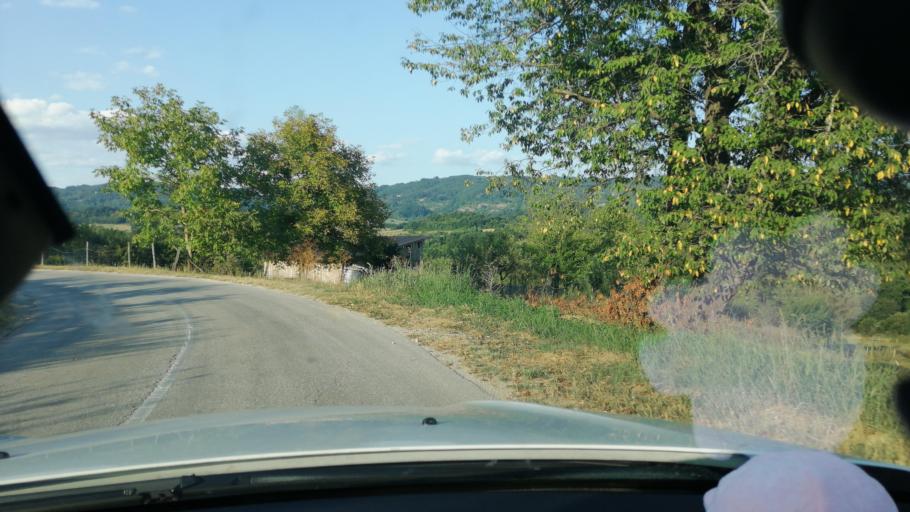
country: RS
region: Central Serbia
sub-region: Moravicki Okrug
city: Cacak
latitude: 43.8170
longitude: 20.2552
